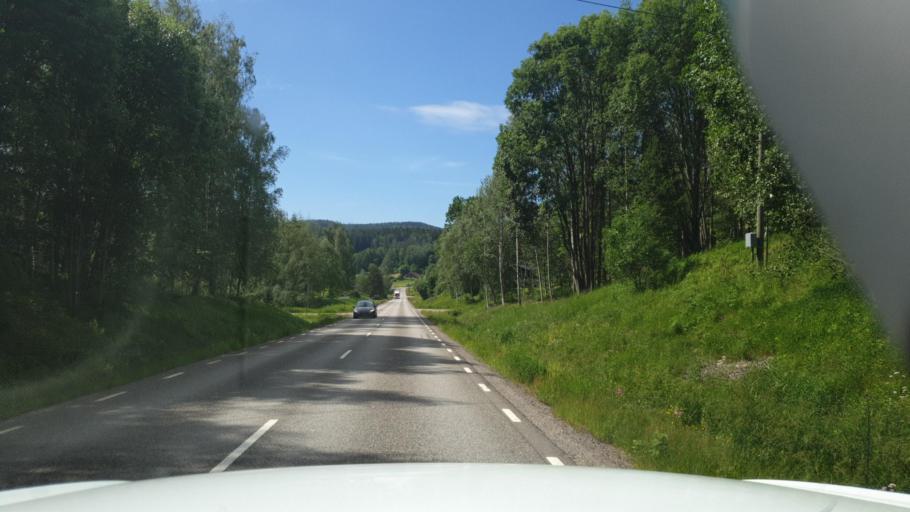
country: SE
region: Vaermland
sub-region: Eda Kommun
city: Amotfors
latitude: 59.6844
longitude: 12.4141
